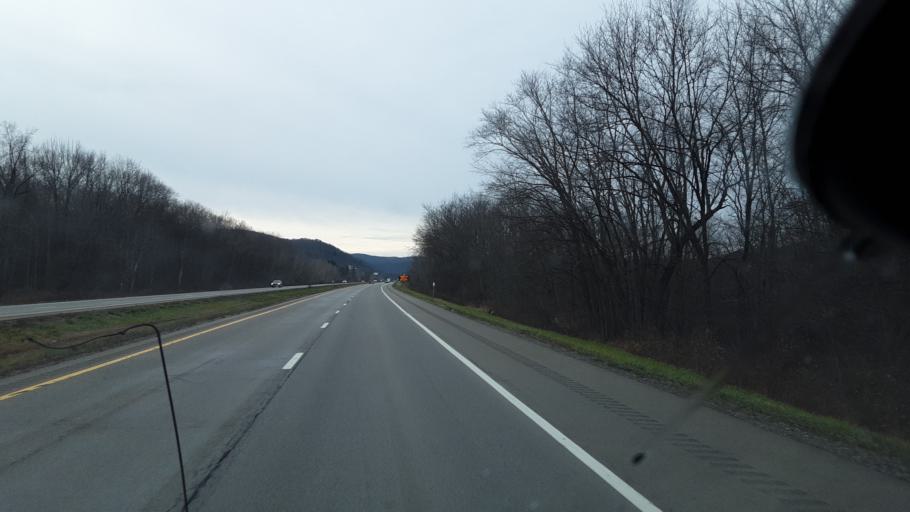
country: US
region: New York
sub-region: Cattaraugus County
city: Allegany
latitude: 42.0867
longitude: -78.5869
